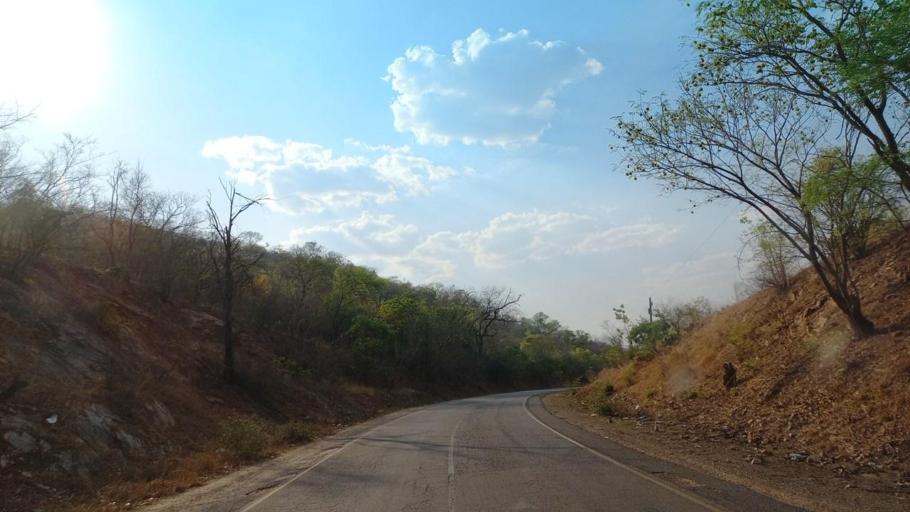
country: ZM
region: Lusaka
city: Luangwa
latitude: -14.9846
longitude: 30.1858
